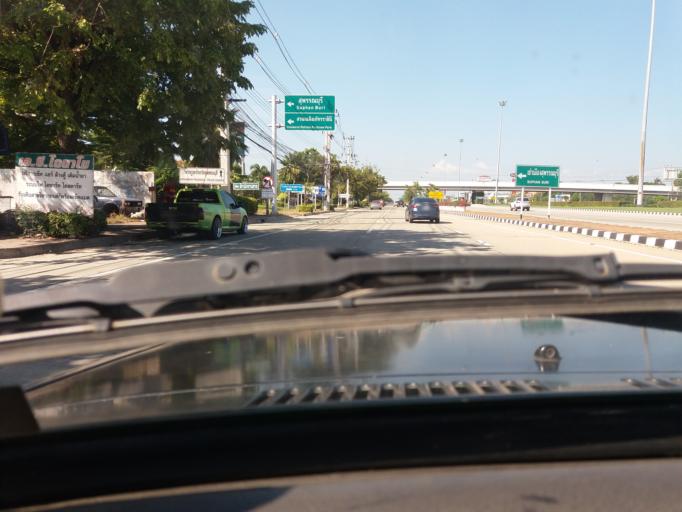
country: TH
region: Suphan Buri
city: Suphan Buri
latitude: 14.4633
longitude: 100.1311
